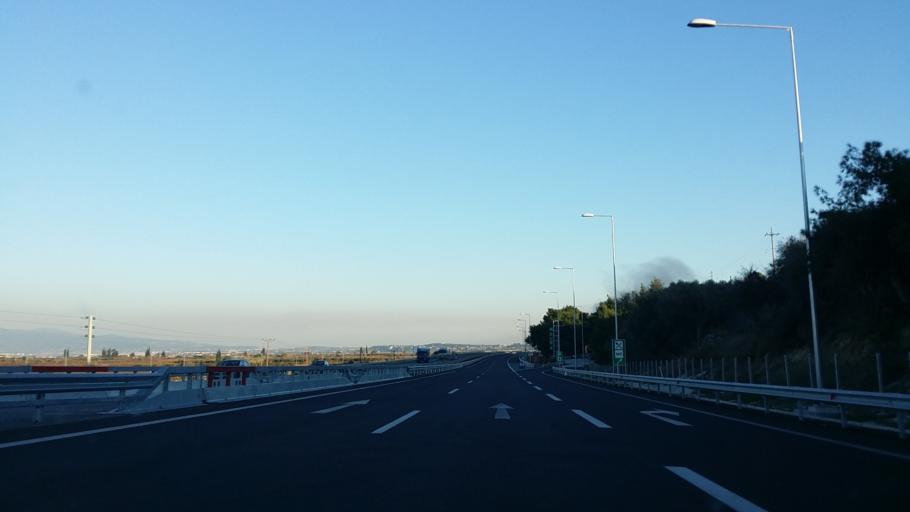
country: GR
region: Peloponnese
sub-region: Nomos Korinthias
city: Zevgolateio
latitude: 37.9217
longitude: 22.8125
